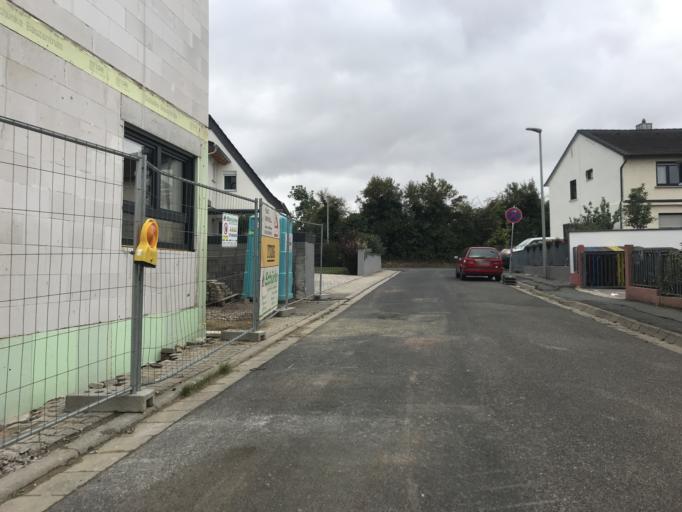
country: DE
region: Rheinland-Pfalz
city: Ober-Saulheim
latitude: 49.8715
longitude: 8.1505
